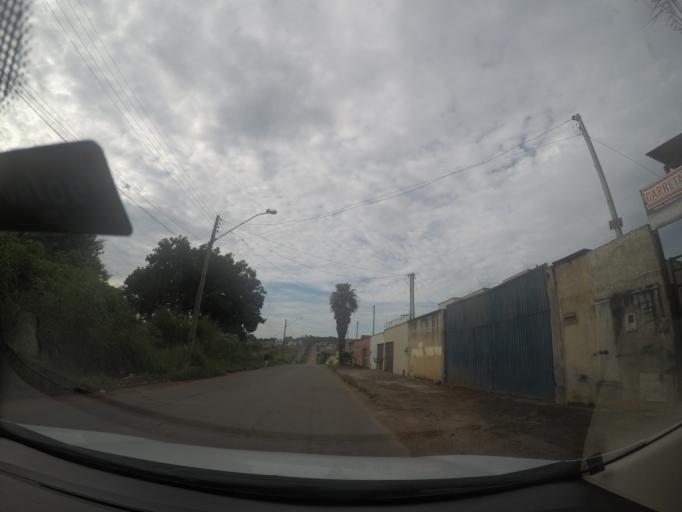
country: BR
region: Goias
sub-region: Goiania
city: Goiania
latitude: -16.6739
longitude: -49.2029
